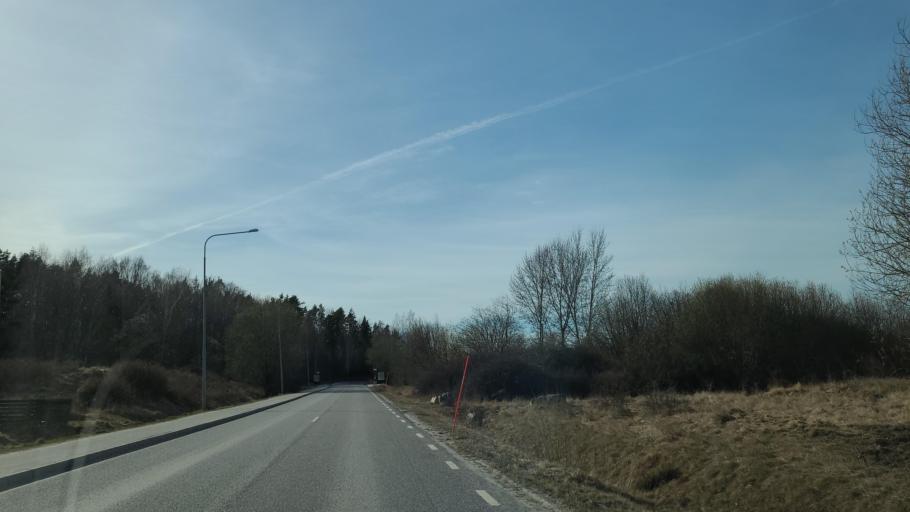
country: SE
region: Stockholm
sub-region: Ekero Kommun
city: Ekeroe
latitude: 59.2799
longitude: 17.7783
